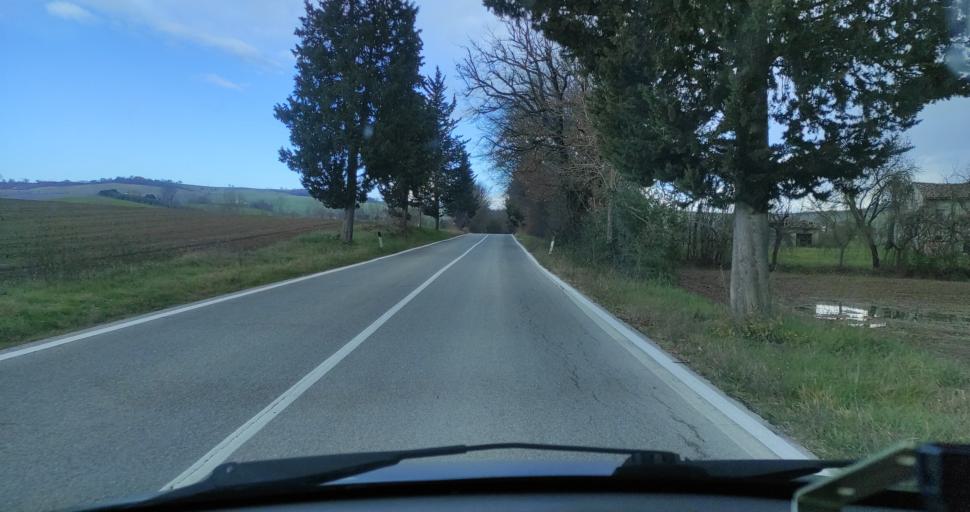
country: IT
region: The Marches
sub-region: Provincia di Macerata
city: Petriolo
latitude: 43.1992
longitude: 13.4462
